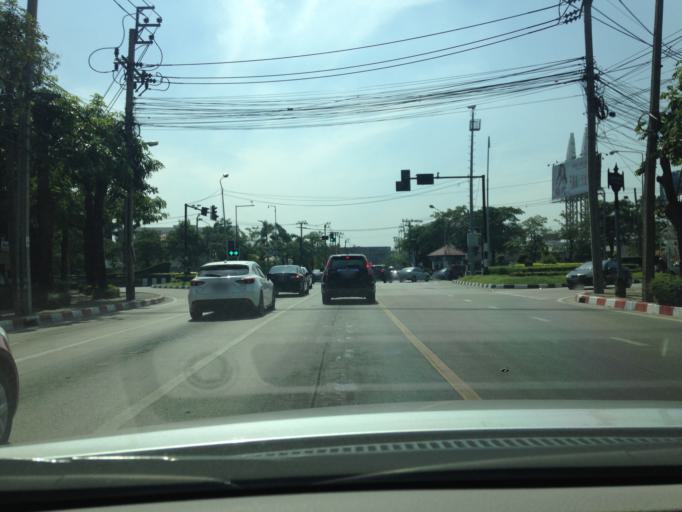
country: TH
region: Bangkok
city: Lat Phrao
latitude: 13.8303
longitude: 100.6235
